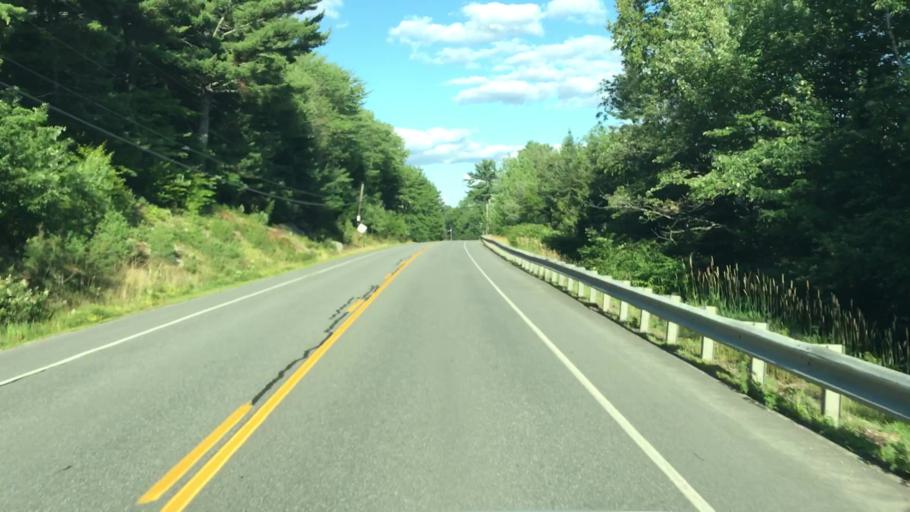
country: US
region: Maine
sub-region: Penobscot County
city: Lincoln
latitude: 45.3744
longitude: -68.4777
